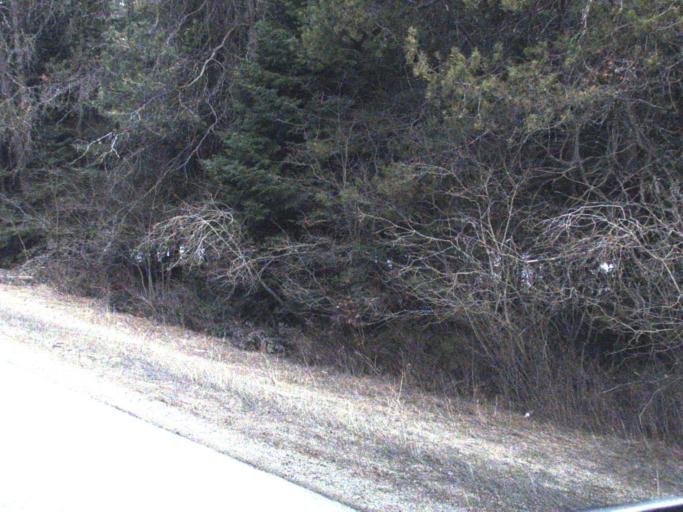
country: US
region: Washington
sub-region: Pend Oreille County
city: Newport
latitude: 48.2271
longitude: -117.1418
